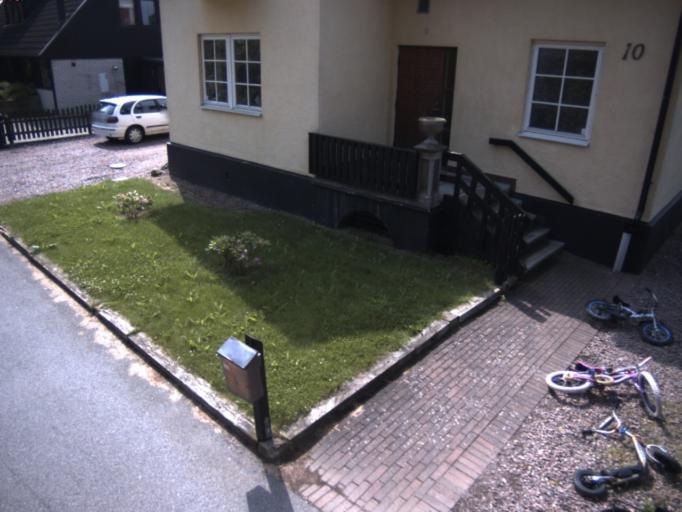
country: SE
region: Skane
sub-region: Angelholms Kommun
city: Strovelstorp
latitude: 56.1392
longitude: 12.8158
